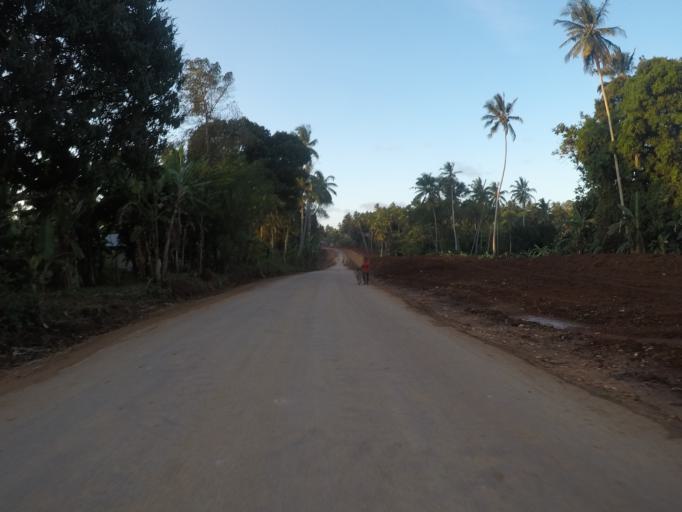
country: TZ
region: Zanzibar North
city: Gamba
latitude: -5.9561
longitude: 39.3061
